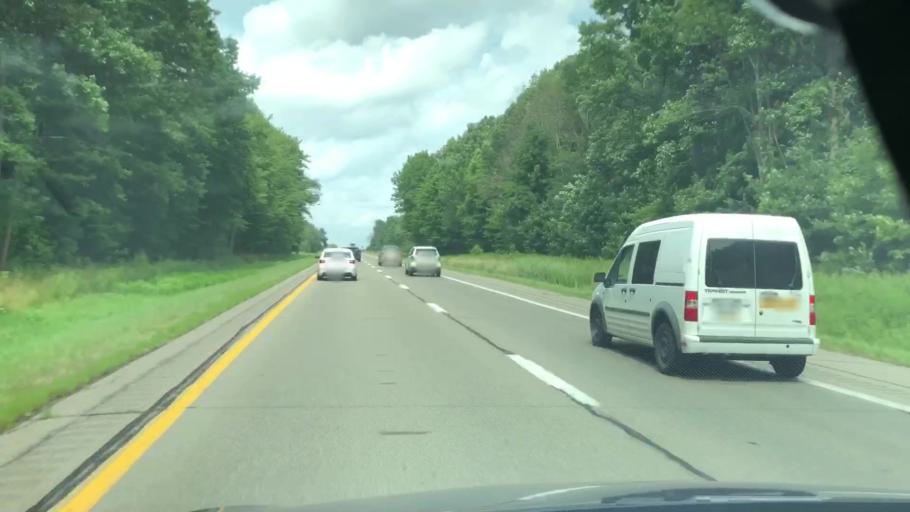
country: US
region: Pennsylvania
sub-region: Crawford County
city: Meadville
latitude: 41.7541
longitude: -80.1963
